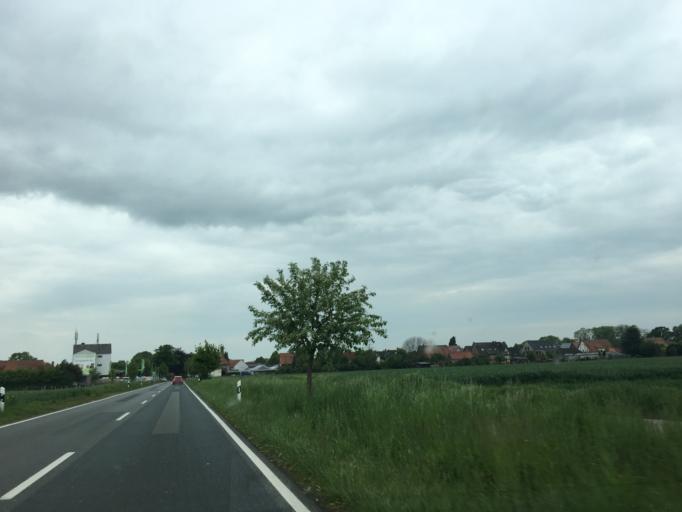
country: DE
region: Lower Saxony
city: Gross Munzel
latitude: 52.3879
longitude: 9.4628
